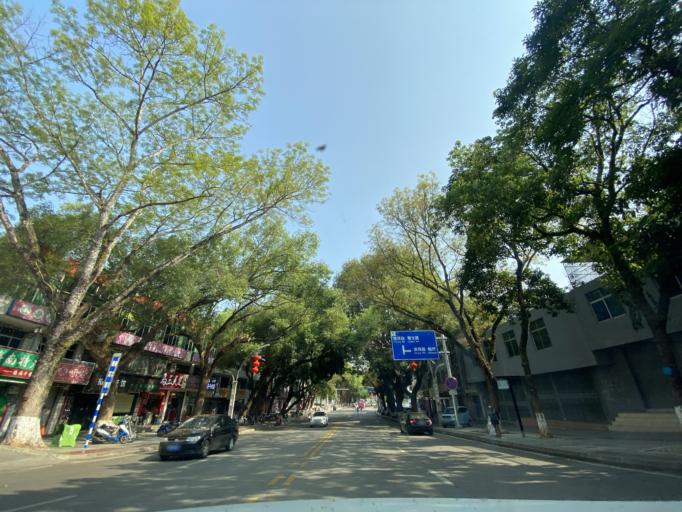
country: CN
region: Hainan
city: Chongshan
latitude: 18.7740
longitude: 109.5153
